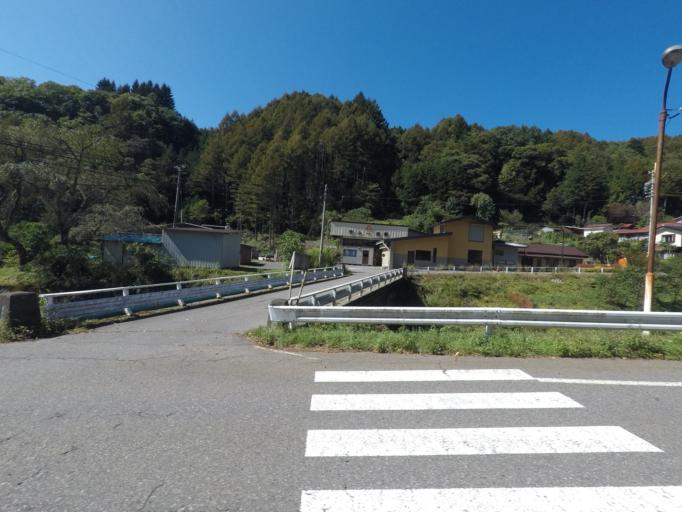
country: JP
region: Nagano
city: Shiojiri
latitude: 35.9904
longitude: 137.7405
